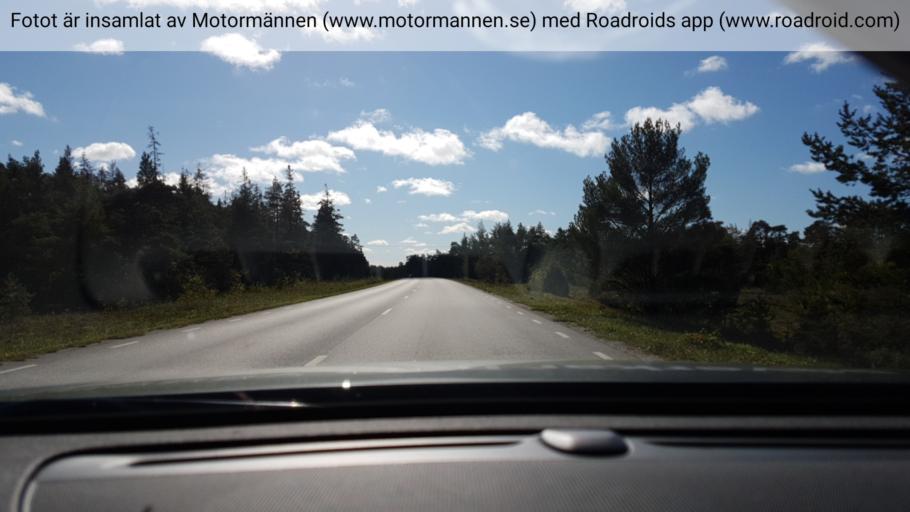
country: SE
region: Gotland
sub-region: Gotland
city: Slite
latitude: 57.7478
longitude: 18.7894
